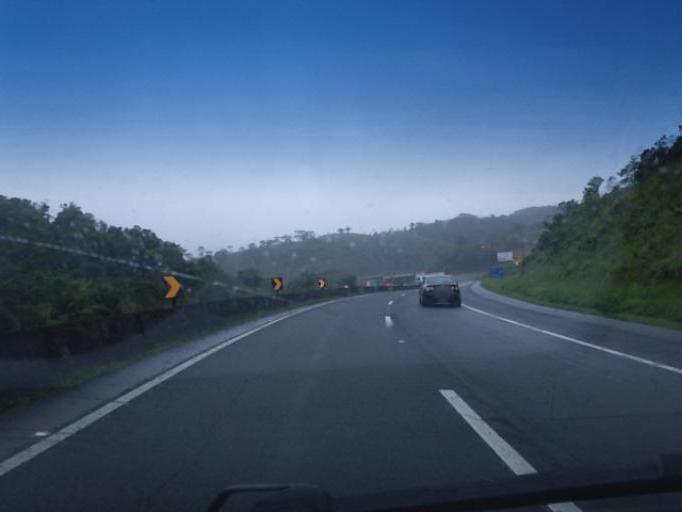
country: BR
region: Parana
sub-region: Antonina
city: Antonina
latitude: -25.0987
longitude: -48.6794
